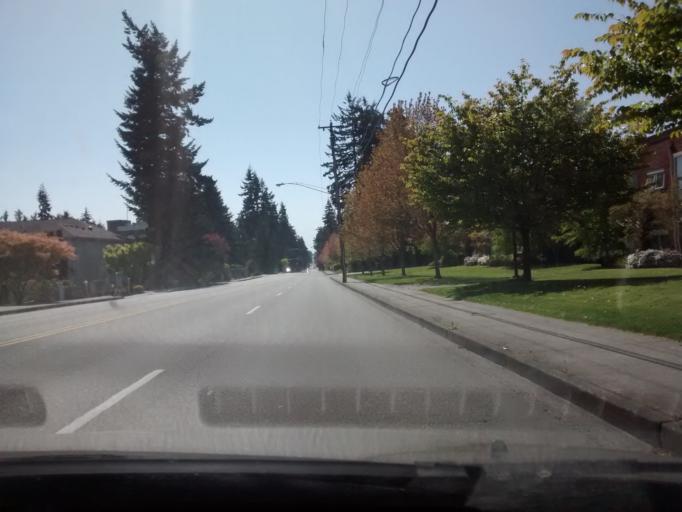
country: US
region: Washington
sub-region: Snohomish County
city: Lynnwood
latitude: 47.8060
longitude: -122.3358
